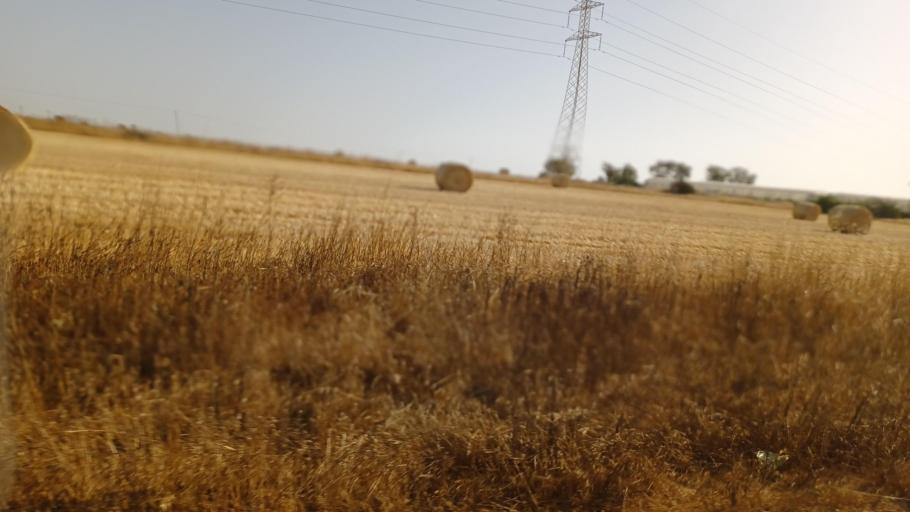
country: CY
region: Ammochostos
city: Liopetri
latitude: 35.0013
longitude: 33.9287
